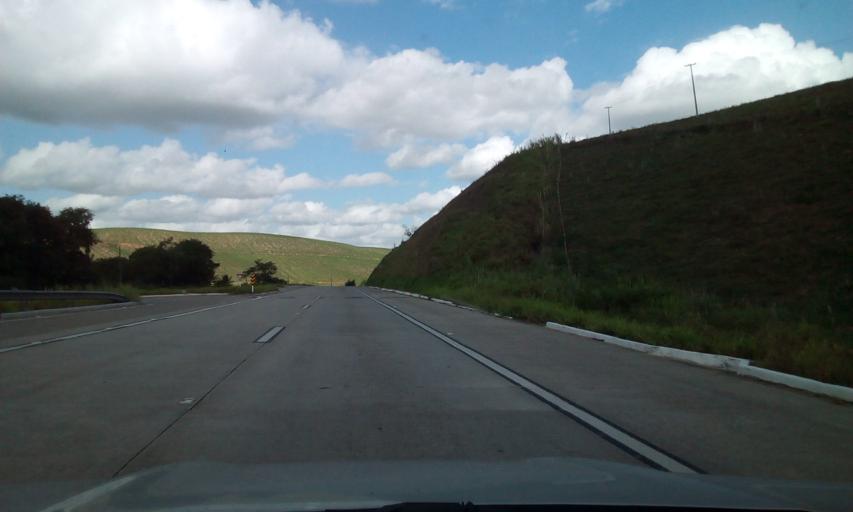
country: BR
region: Alagoas
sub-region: Novo Lino
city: Novo Lino
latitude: -8.9381
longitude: -35.6553
